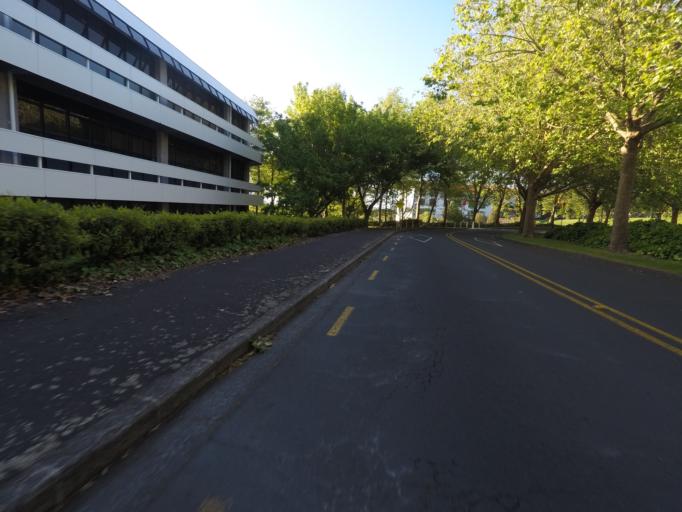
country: NZ
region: Auckland
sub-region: Auckland
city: Rosebank
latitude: -36.8813
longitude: 174.7097
